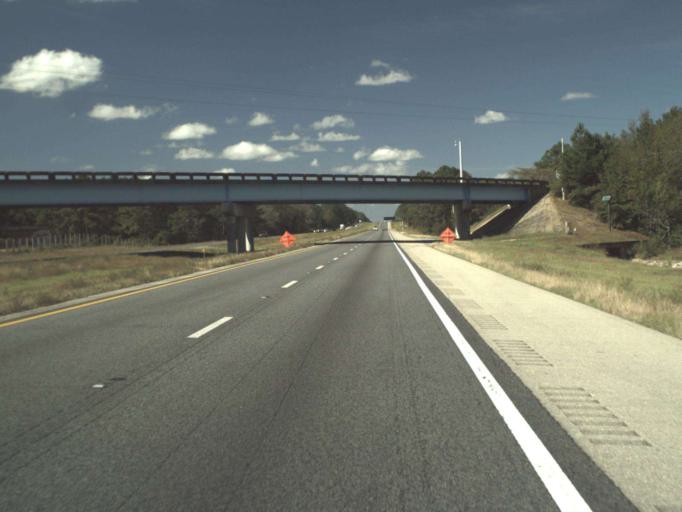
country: US
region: Florida
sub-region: Washington County
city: Chipley
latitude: 30.7464
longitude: -85.5086
